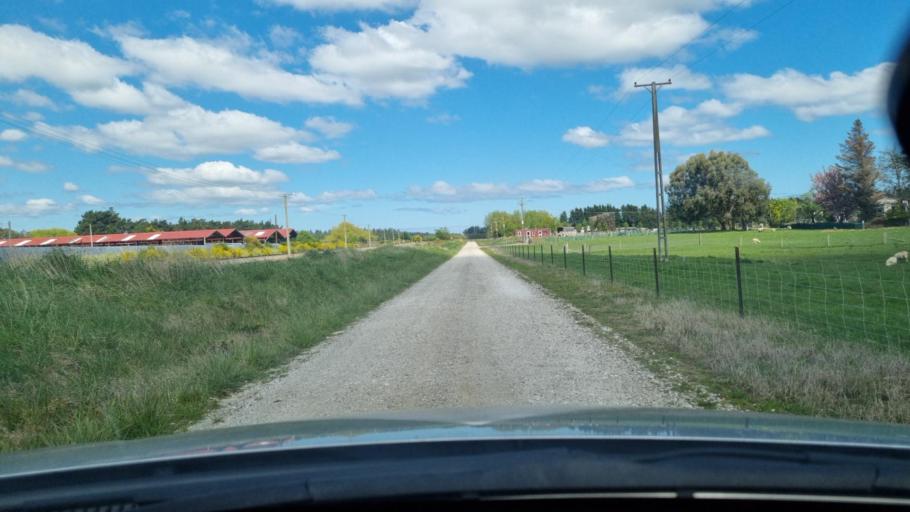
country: NZ
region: Southland
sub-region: Invercargill City
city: Invercargill
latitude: -46.3458
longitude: 168.3400
